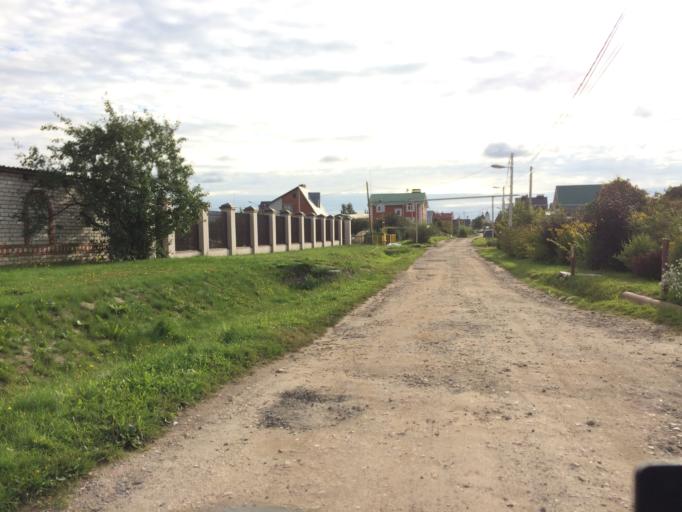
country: RU
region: Mariy-El
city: Yoshkar-Ola
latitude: 56.6536
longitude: 47.9909
